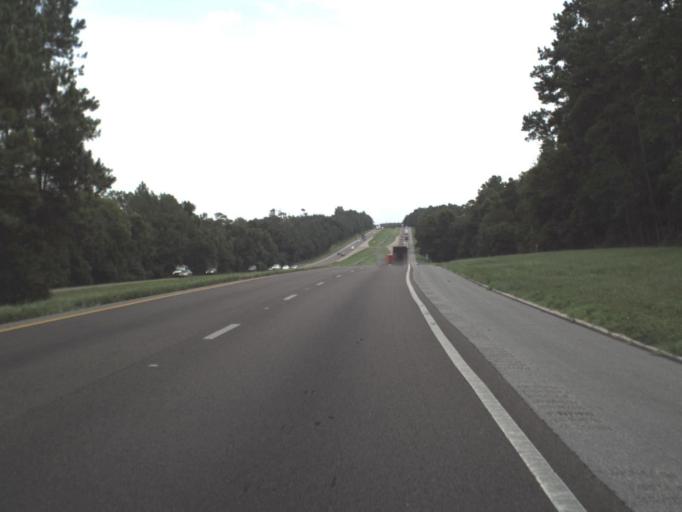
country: US
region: Florida
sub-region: Hernando County
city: Hill 'n Dale
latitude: 28.4669
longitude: -82.2714
